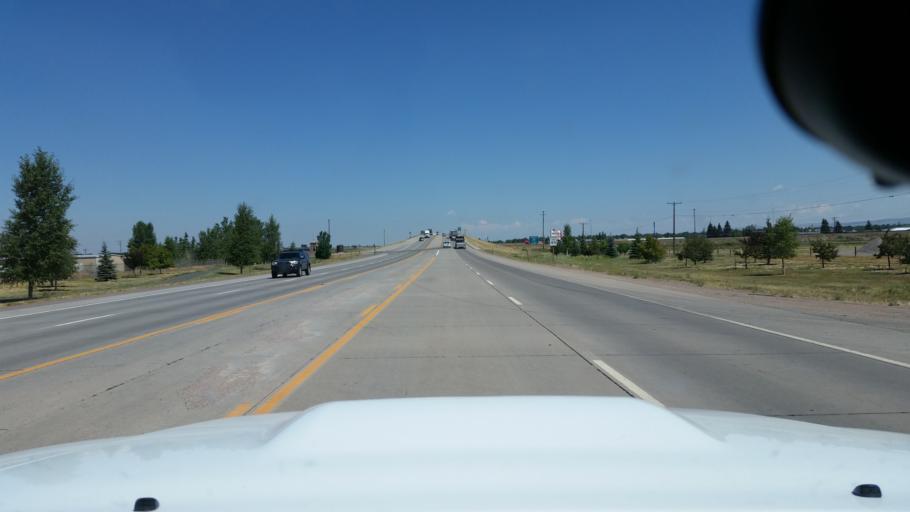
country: US
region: Wyoming
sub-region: Albany County
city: Laramie
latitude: 41.2873
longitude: -105.5926
